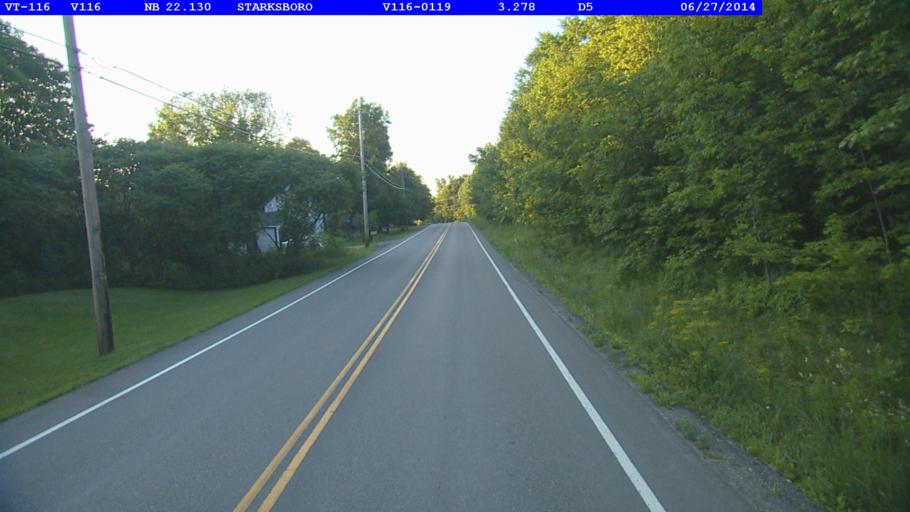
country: US
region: Vermont
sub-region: Addison County
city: Bristol
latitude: 44.2319
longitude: -73.0568
